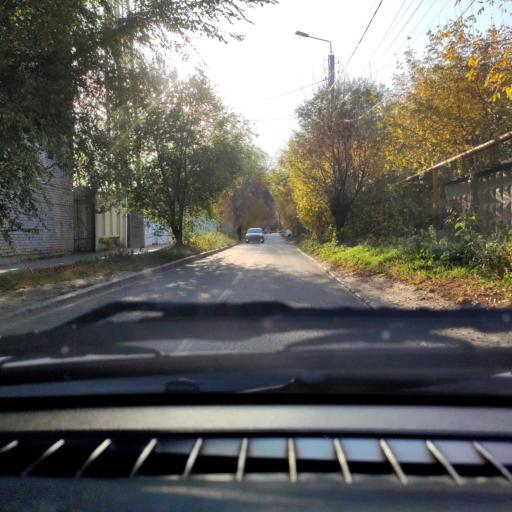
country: RU
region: Samara
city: Tol'yatti
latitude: 53.5135
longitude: 49.4042
